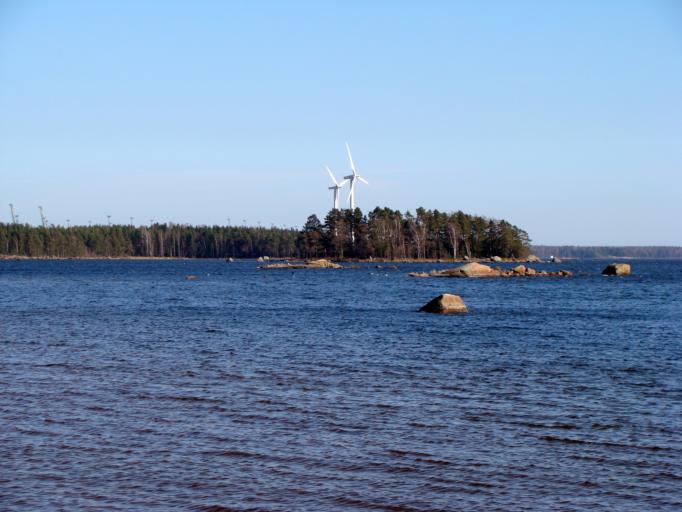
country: FI
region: Kymenlaakso
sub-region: Kotka-Hamina
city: Kotka
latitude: 60.4361
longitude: 26.8645
